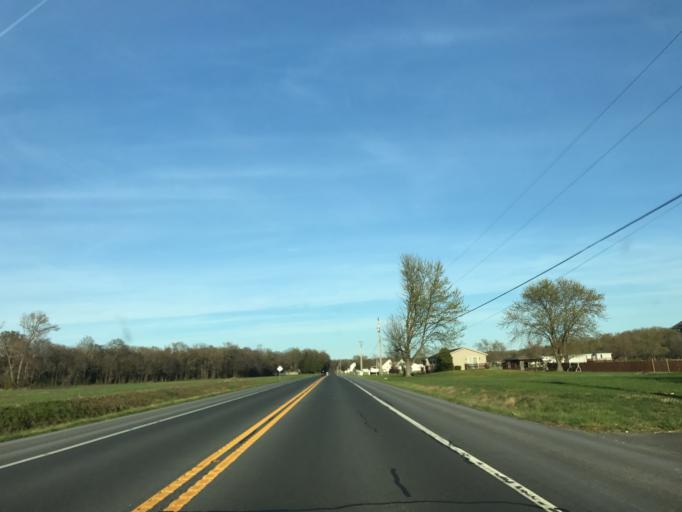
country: US
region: Delaware
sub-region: Kent County
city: Cheswold
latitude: 39.1471
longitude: -75.6697
